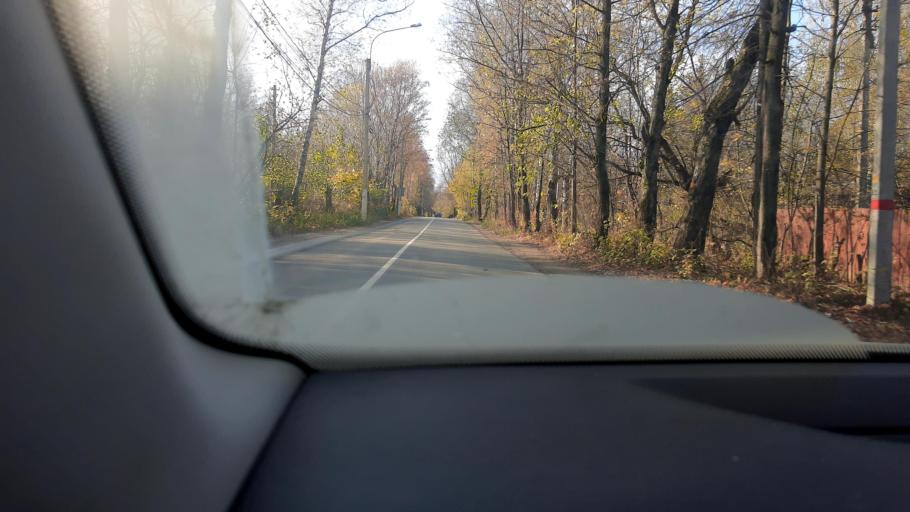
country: RU
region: Moskovskaya
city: Shcherbinka
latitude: 55.5305
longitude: 37.6026
